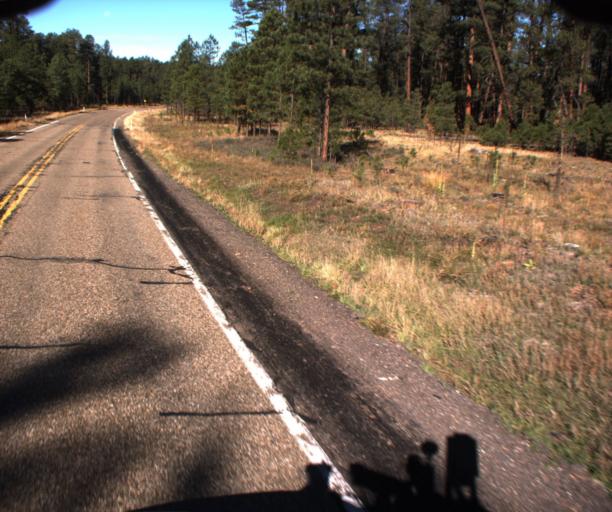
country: US
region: Arizona
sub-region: Coconino County
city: Fredonia
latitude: 36.7440
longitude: -112.2403
